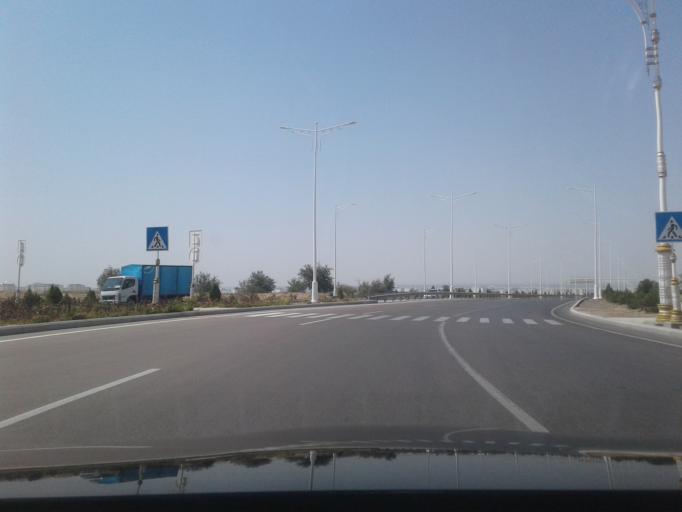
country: TM
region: Ahal
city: Ashgabat
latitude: 37.8786
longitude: 58.4227
